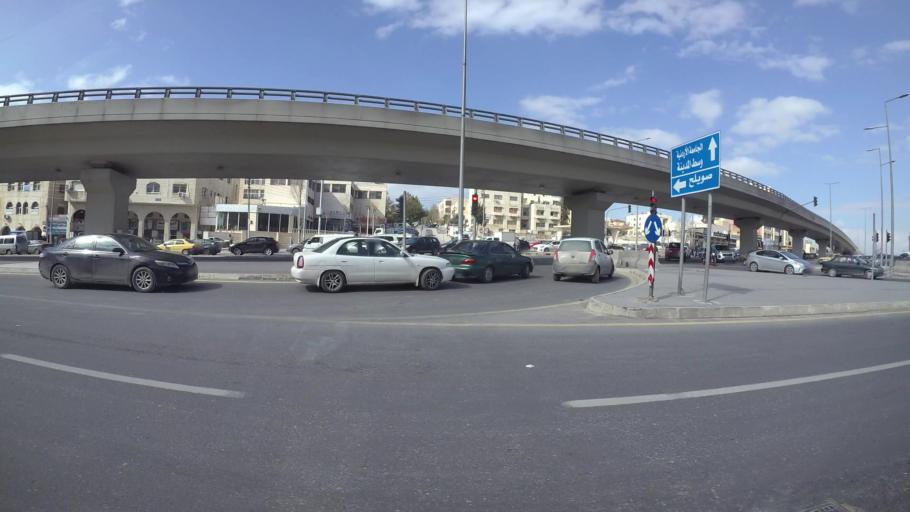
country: JO
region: Amman
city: Al Jubayhah
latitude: 32.0243
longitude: 35.8542
